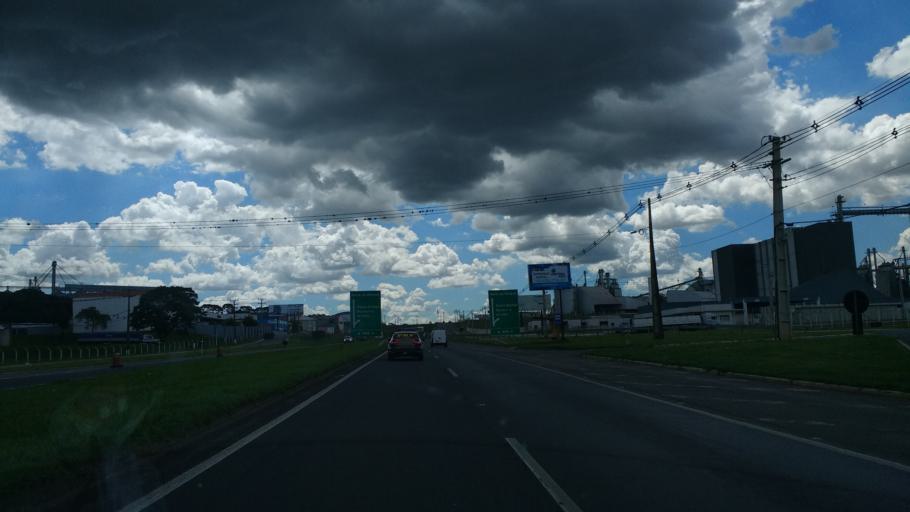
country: BR
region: Parana
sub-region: Ponta Grossa
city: Ponta Grossa
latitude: -25.1546
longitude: -50.1350
